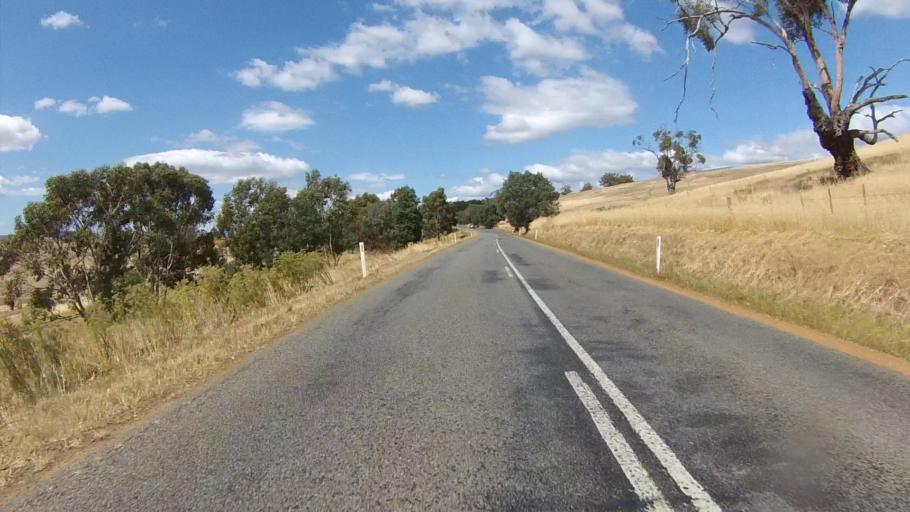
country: AU
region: Tasmania
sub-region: Derwent Valley
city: New Norfolk
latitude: -42.6856
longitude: 146.8695
